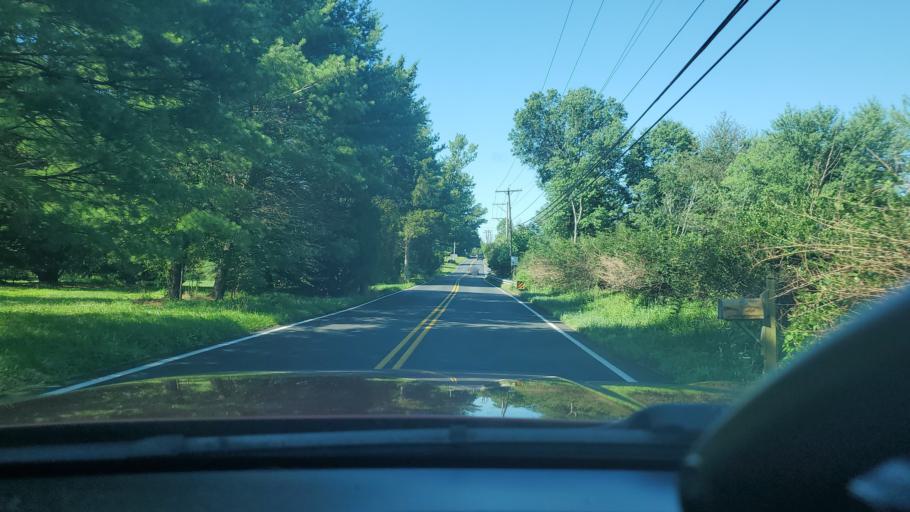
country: US
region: Pennsylvania
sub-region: Montgomery County
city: Limerick
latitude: 40.2511
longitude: -75.5269
